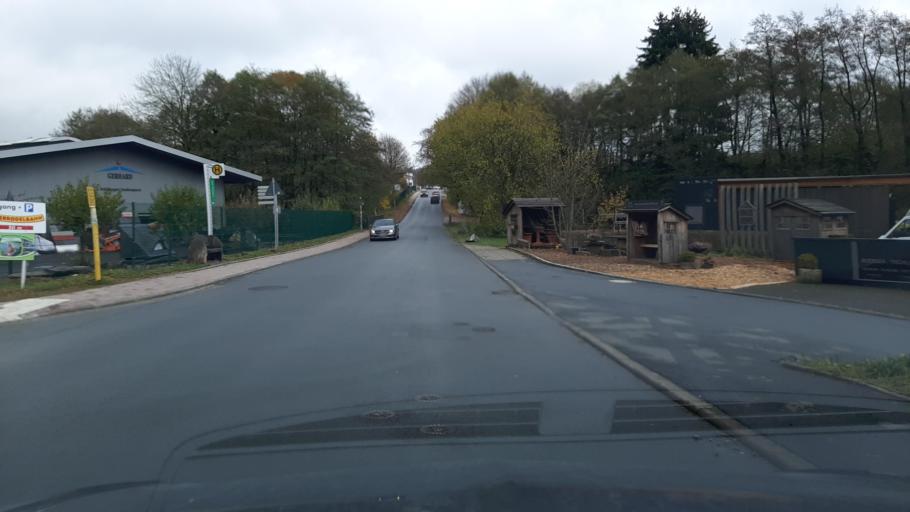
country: DE
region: Hesse
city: Willingen
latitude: 51.2926
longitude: 8.5967
